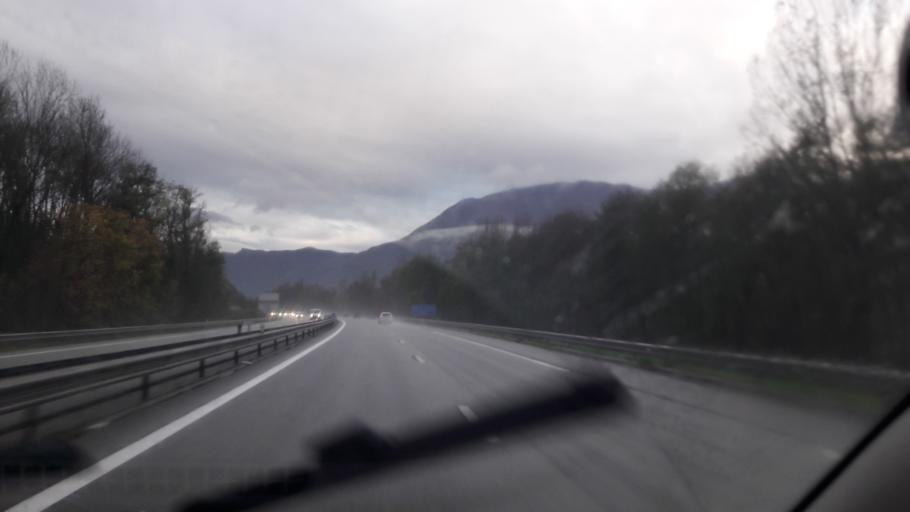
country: FR
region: Rhone-Alpes
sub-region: Departement de la Savoie
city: Coise-Saint-Jean-Pied-Gauthier
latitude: 45.5571
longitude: 6.1871
